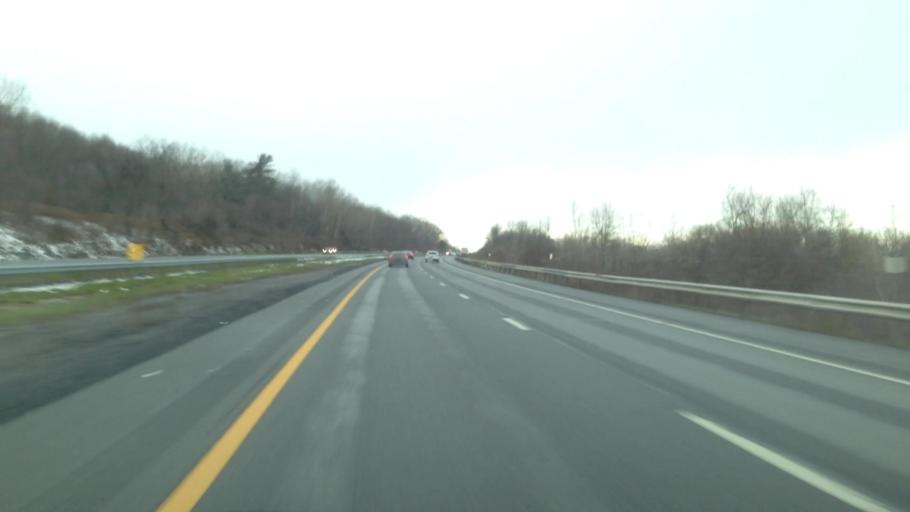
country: US
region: New York
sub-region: Montgomery County
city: Saint Johnsville
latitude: 42.9914
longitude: -74.7319
